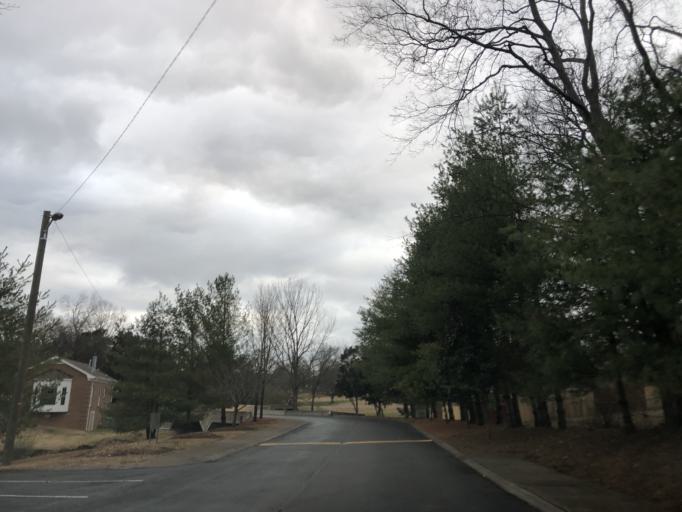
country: US
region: Tennessee
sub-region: Davidson County
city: Goodlettsville
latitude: 36.2954
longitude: -86.6871
